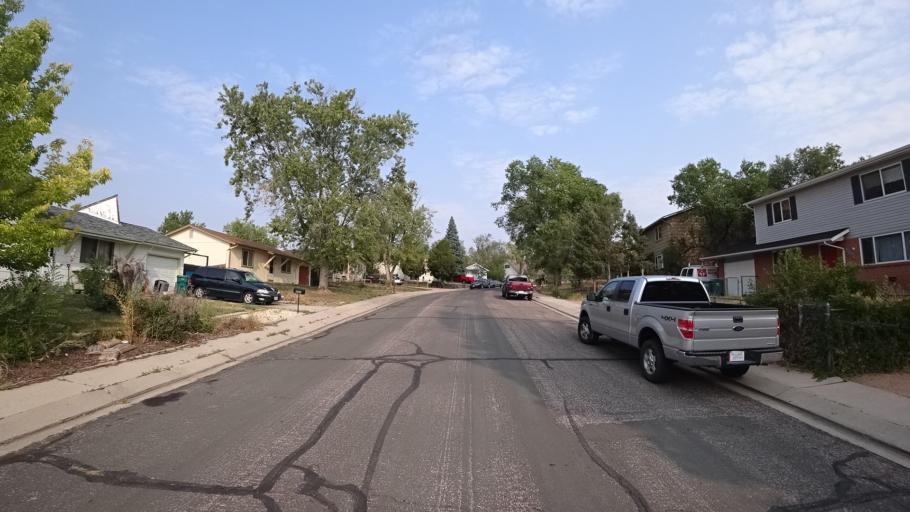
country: US
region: Colorado
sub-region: El Paso County
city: Stratmoor
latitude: 38.8014
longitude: -104.7645
